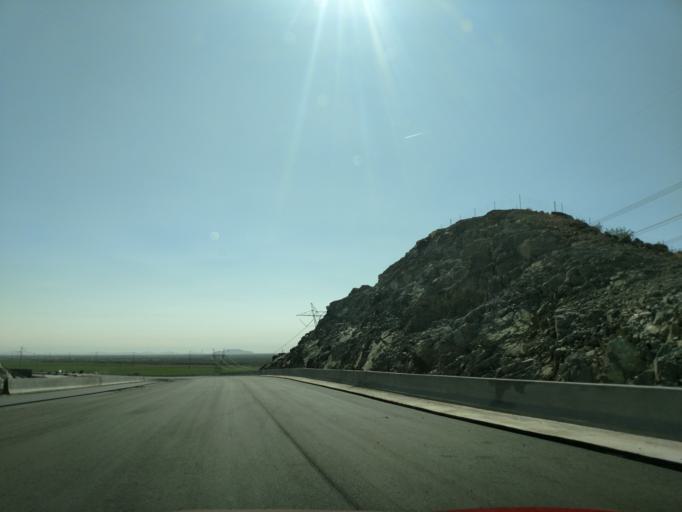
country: US
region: Arizona
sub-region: Maricopa County
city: Laveen
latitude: 33.2954
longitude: -112.1371
